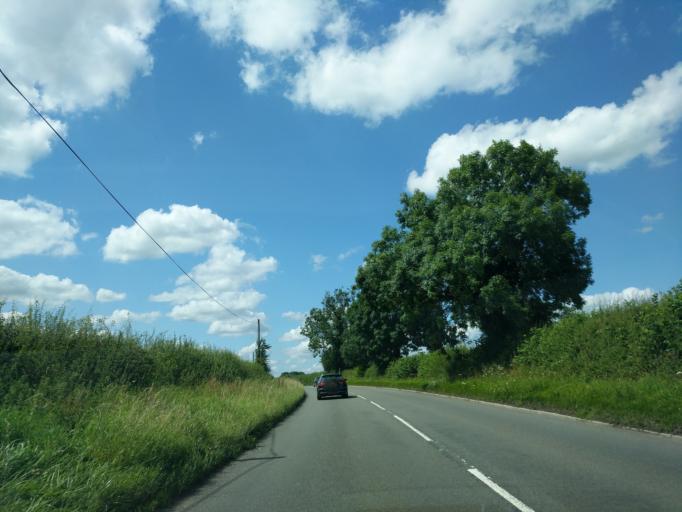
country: GB
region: England
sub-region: Staffordshire
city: Uttoxeter
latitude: 52.9314
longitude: -1.9256
